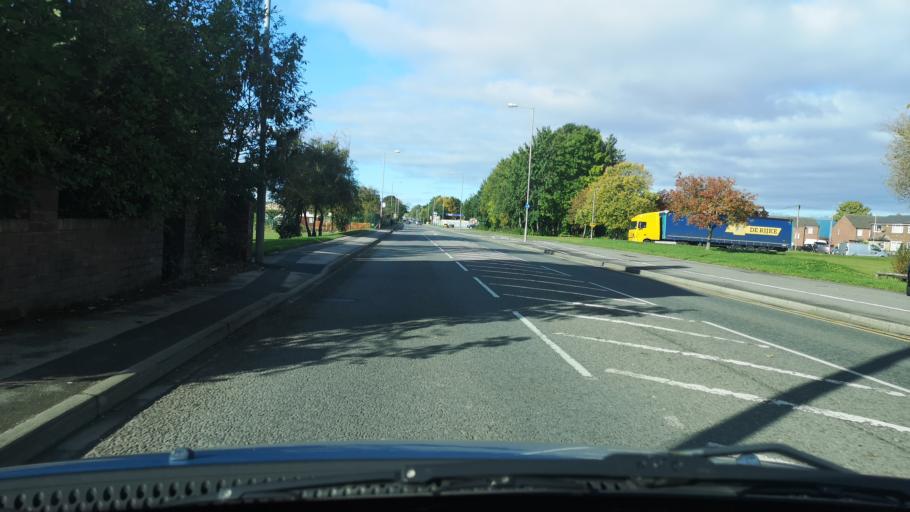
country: GB
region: England
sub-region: City and Borough of Wakefield
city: Featherstone
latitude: 53.6751
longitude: -1.3634
